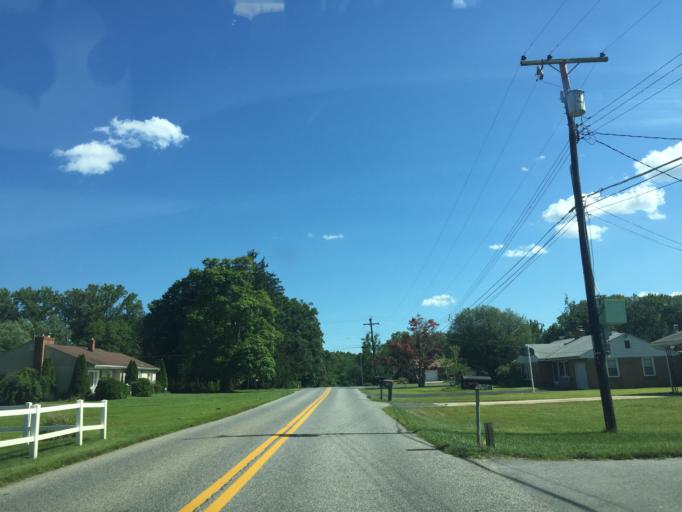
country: US
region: Maryland
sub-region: Baltimore County
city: White Marsh
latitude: 39.4131
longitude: -76.4180
